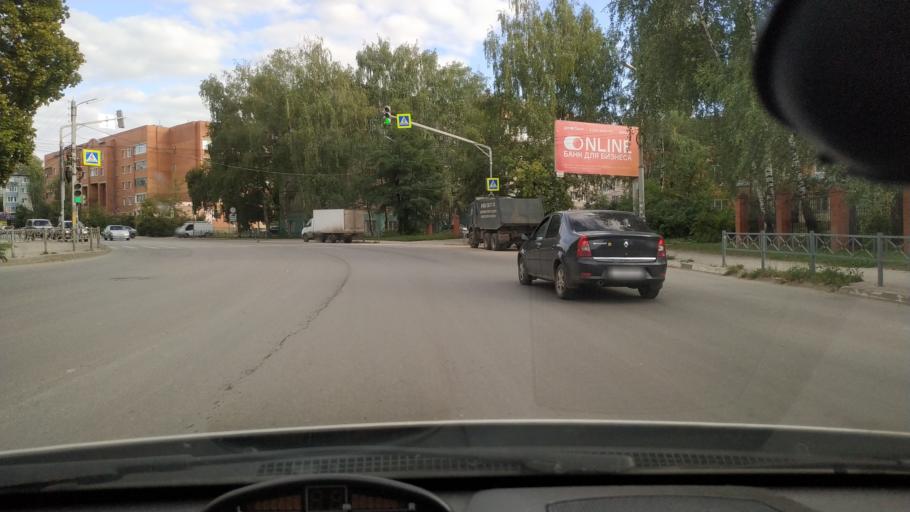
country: RU
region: Rjazan
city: Ryazan'
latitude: 54.6061
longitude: 39.7047
